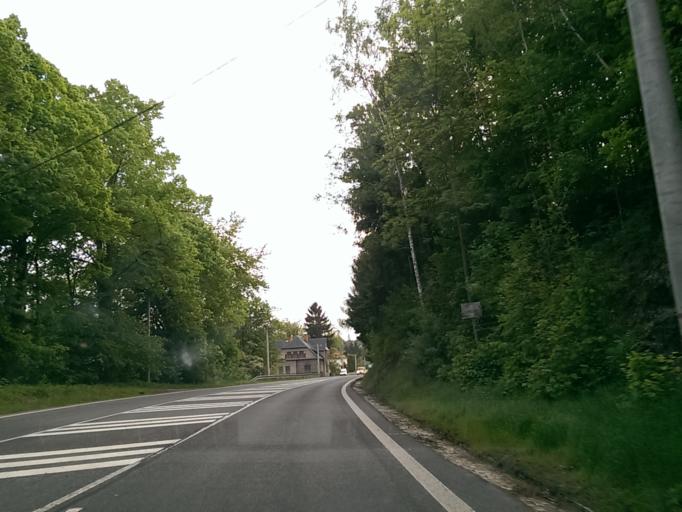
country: CZ
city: Plavy
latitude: 50.6922
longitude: 15.3153
